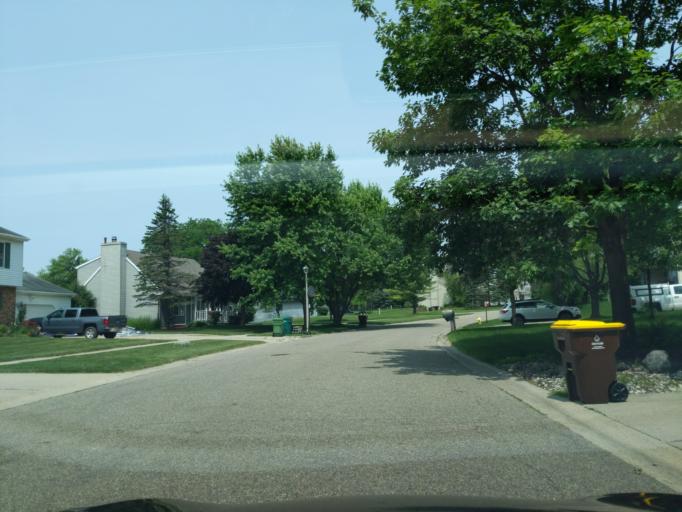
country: US
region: Michigan
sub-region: Eaton County
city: Waverly
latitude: 42.7572
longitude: -84.6445
